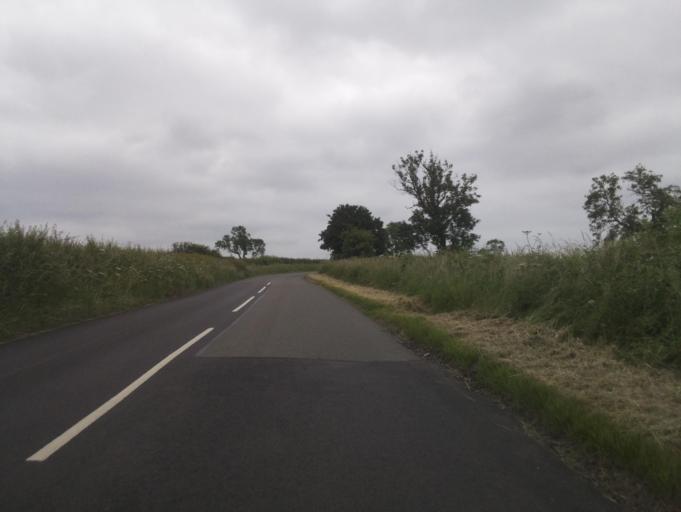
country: GB
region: England
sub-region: Leicestershire
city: Melton Mowbray
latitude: 52.7073
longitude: -0.8335
